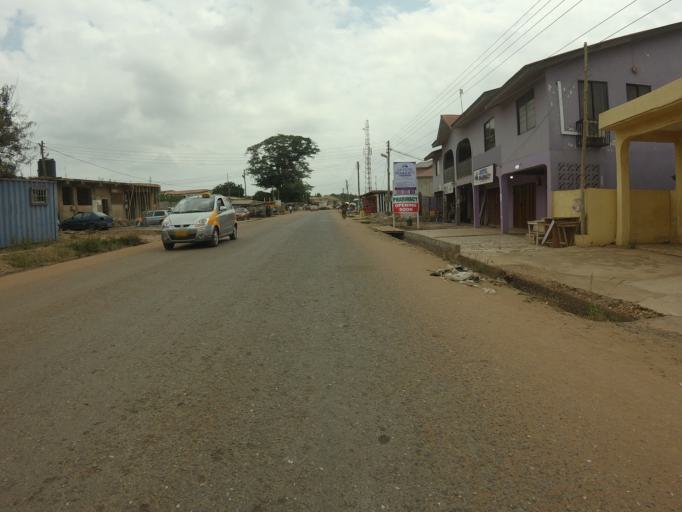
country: GH
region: Greater Accra
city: Dome
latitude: 5.6506
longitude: -0.2607
